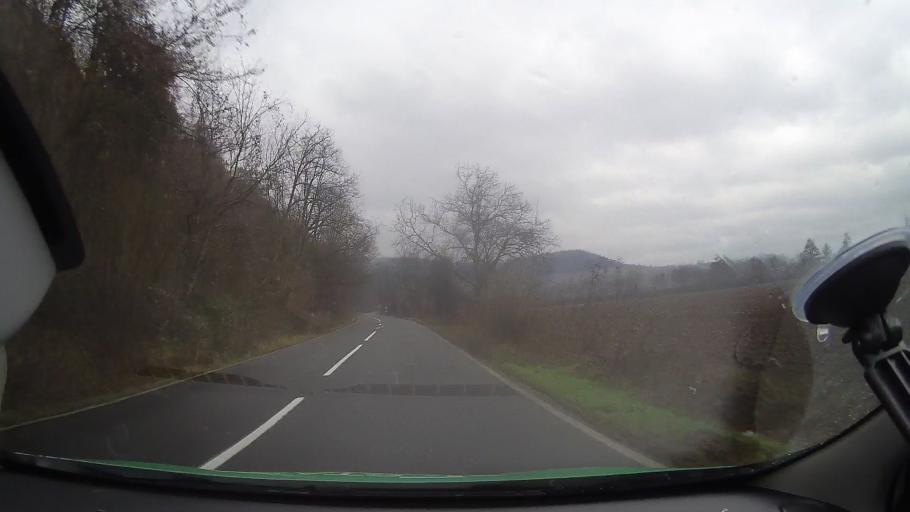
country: RO
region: Arad
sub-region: Comuna Gurahont
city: Gurahont
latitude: 46.2740
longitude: 22.3509
